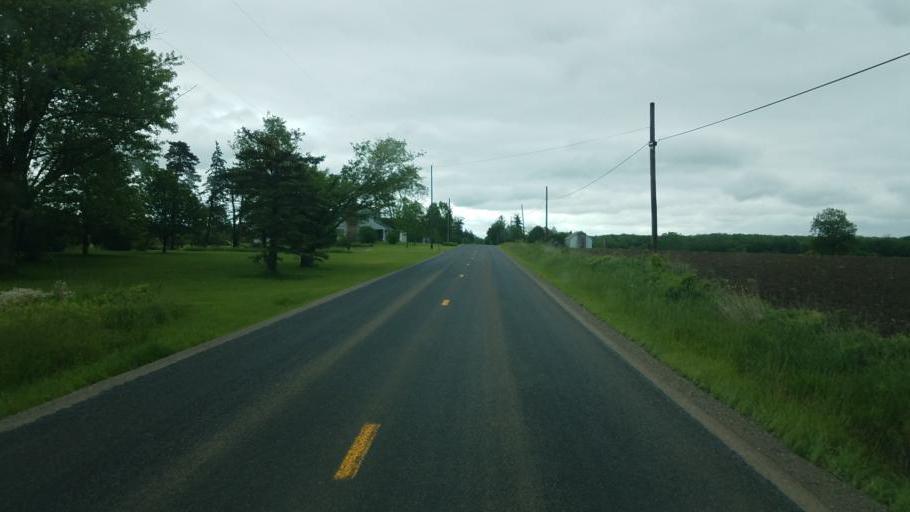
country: US
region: Ohio
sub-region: Medina County
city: Medina
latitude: 41.1809
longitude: -81.9581
